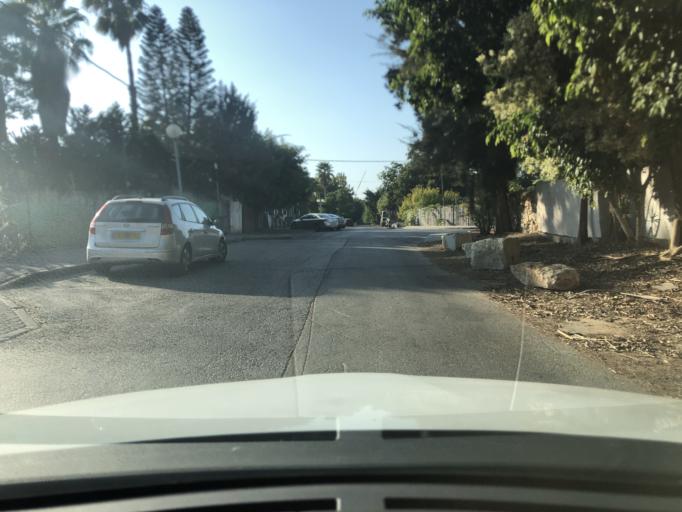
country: IL
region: Central District
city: Hod HaSharon
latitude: 32.1417
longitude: 34.9017
